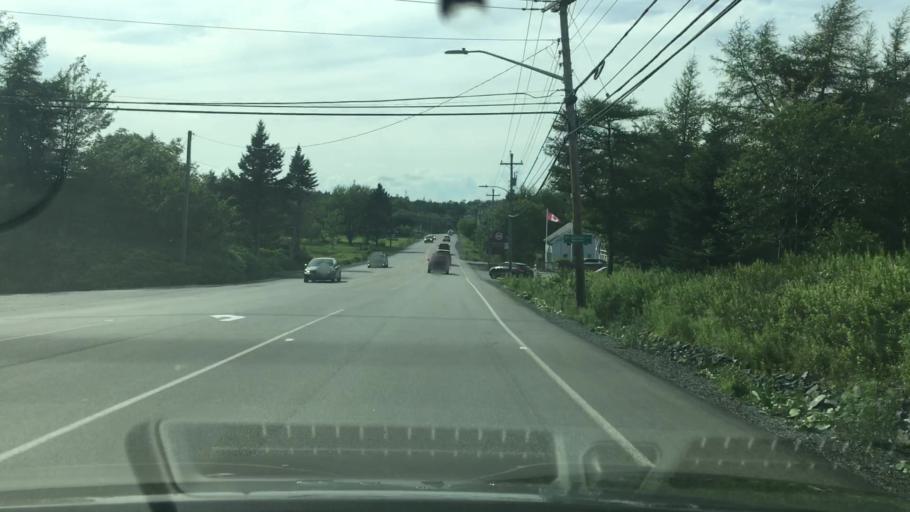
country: CA
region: Nova Scotia
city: Dartmouth
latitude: 44.7268
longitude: -63.7437
